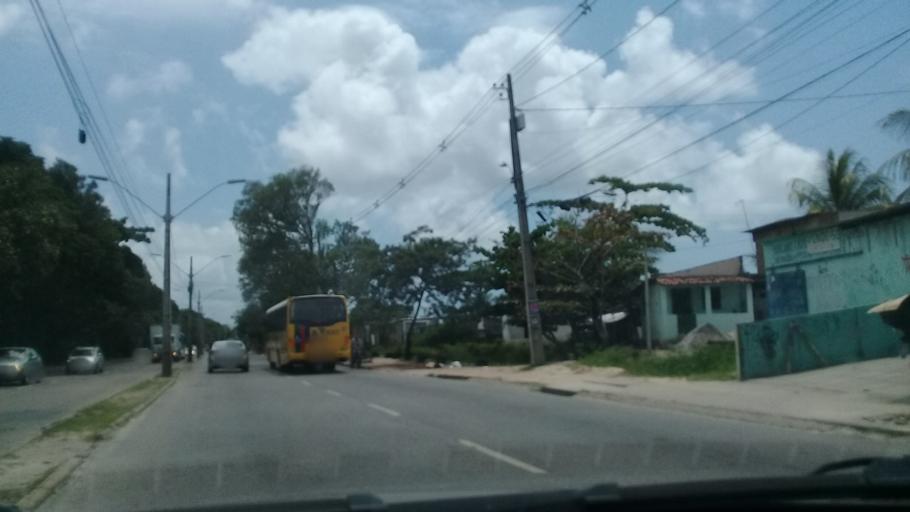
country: BR
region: Pernambuco
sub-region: Recife
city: Recife
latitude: -8.1080
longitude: -34.9317
